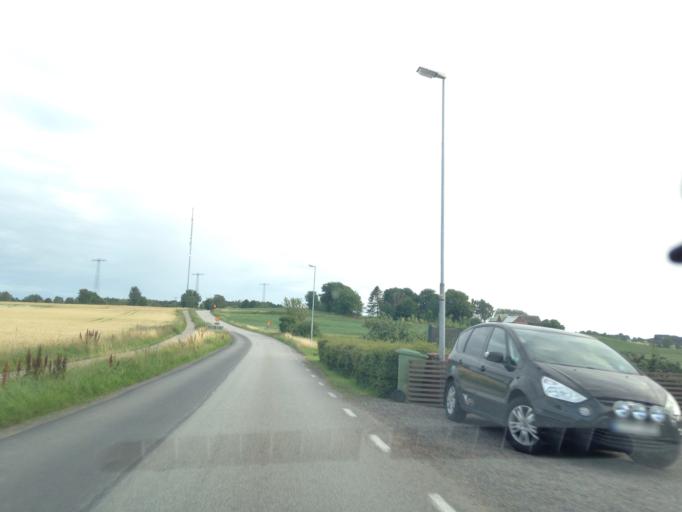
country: SE
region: Halland
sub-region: Varbergs Kommun
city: Tvaaker
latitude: 57.1227
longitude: 12.3919
